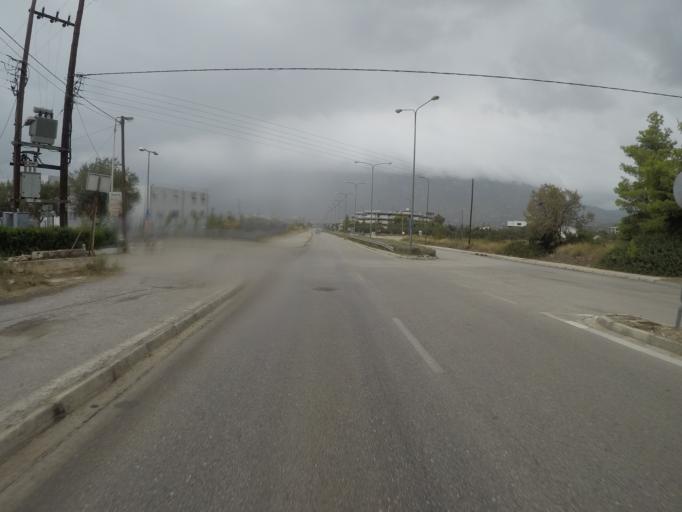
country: GR
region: Peloponnese
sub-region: Nomos Korinthias
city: Korinthos
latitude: 37.9452
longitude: 22.9791
